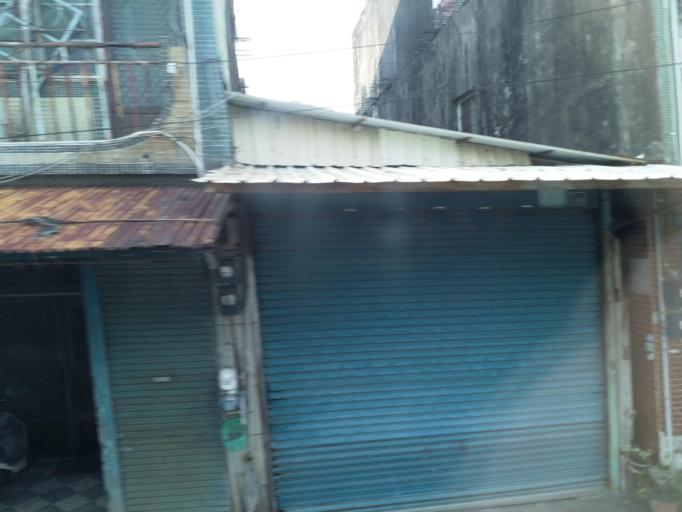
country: TW
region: Taiwan
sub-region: Pingtung
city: Pingtung
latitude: 22.8975
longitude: 120.5212
